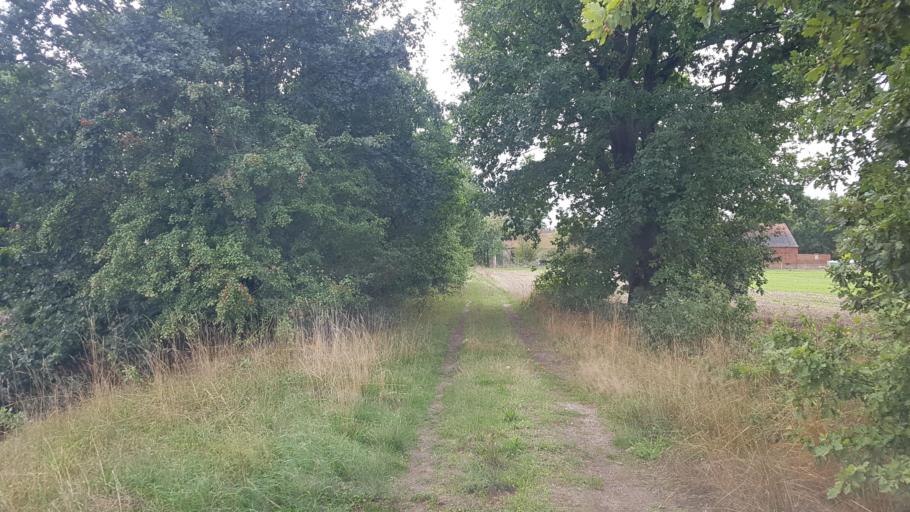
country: DE
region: Brandenburg
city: Schonewalde
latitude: 51.6393
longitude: 13.6055
